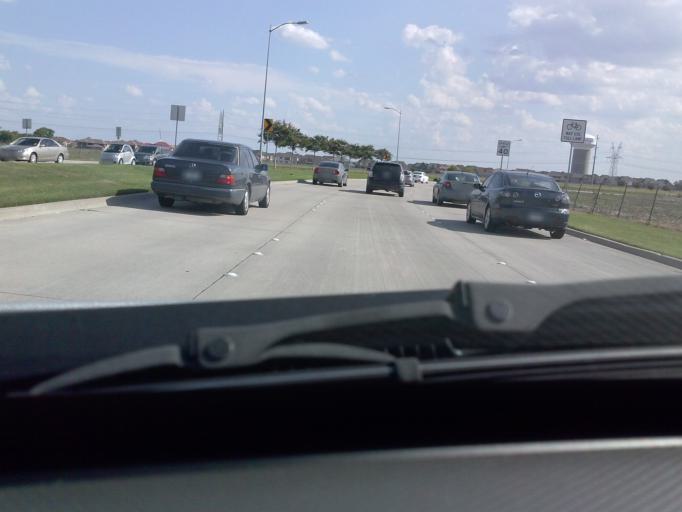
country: US
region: Texas
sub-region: Denton County
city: The Colony
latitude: 33.0652
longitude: -96.8187
